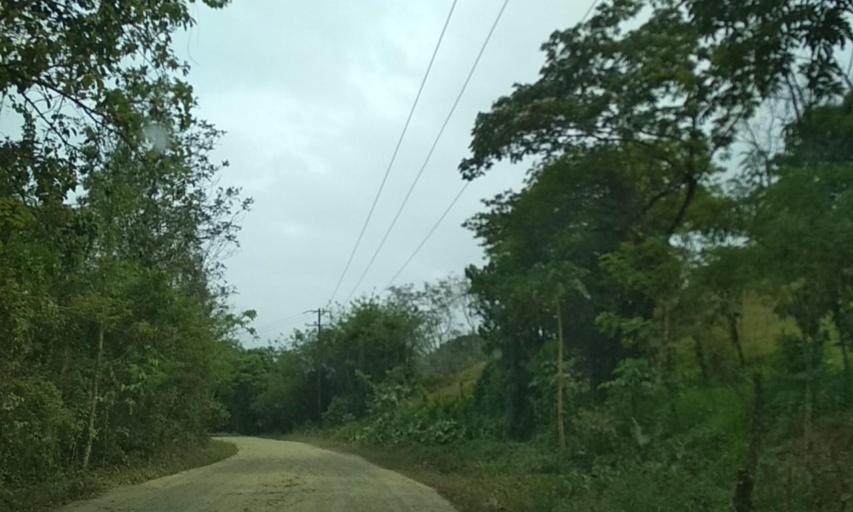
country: MX
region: Veracruz
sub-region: Uxpanapa
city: Poblado 10
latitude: 17.4568
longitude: -94.0975
